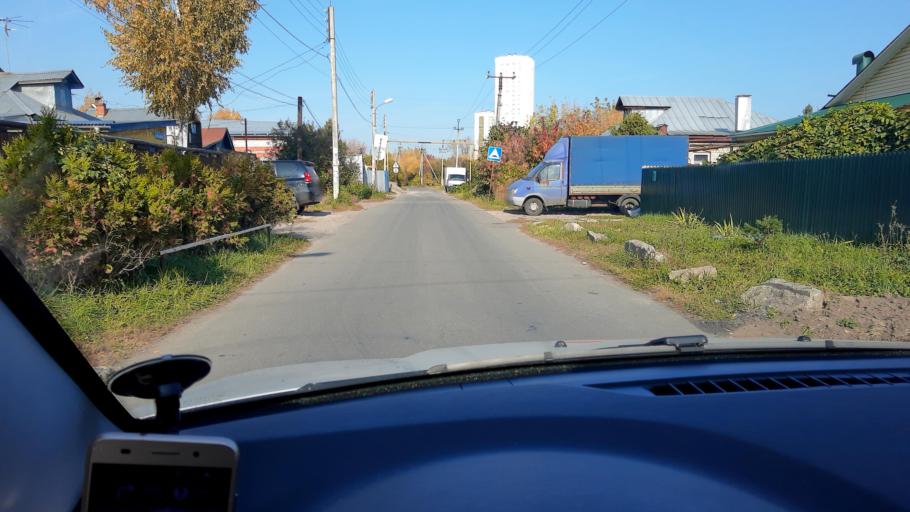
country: RU
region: Nizjnij Novgorod
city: Nizhniy Novgorod
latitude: 56.2984
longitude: 43.9196
